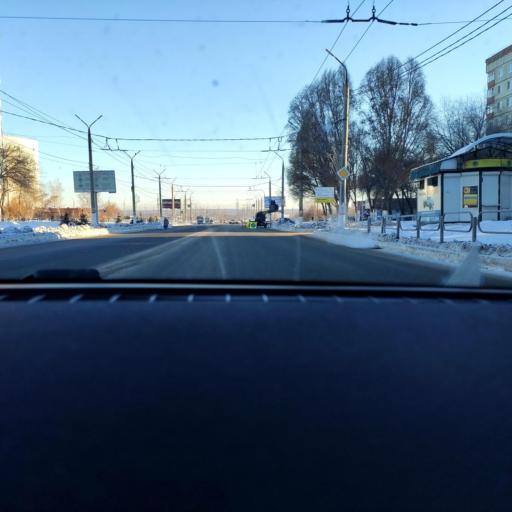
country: RU
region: Samara
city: Novokuybyshevsk
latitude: 53.0892
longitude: 49.9900
